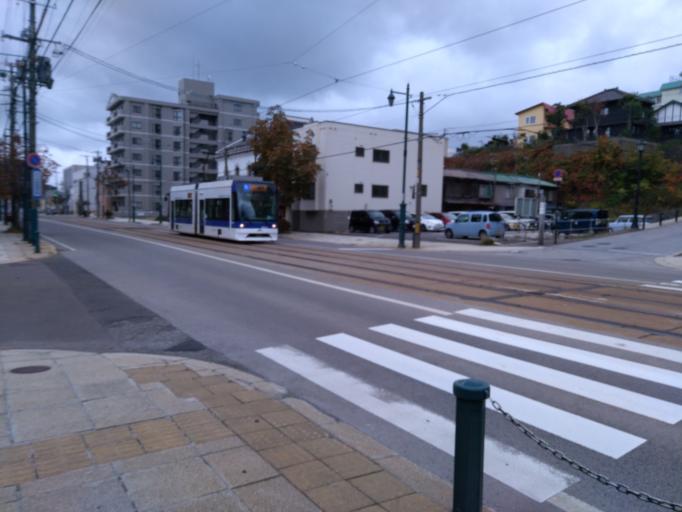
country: JP
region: Hokkaido
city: Hakodate
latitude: 41.7666
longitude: 140.7126
